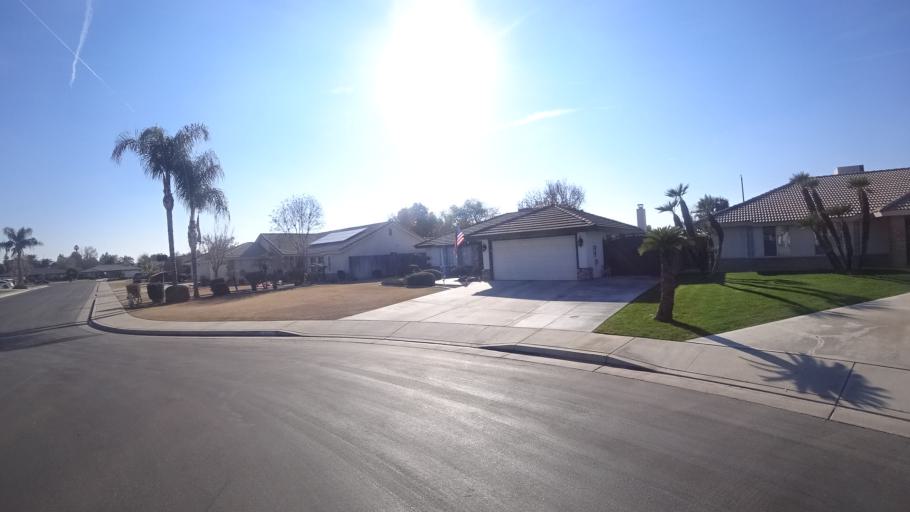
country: US
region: California
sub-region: Kern County
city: Greenacres
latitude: 35.3196
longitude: -119.1053
